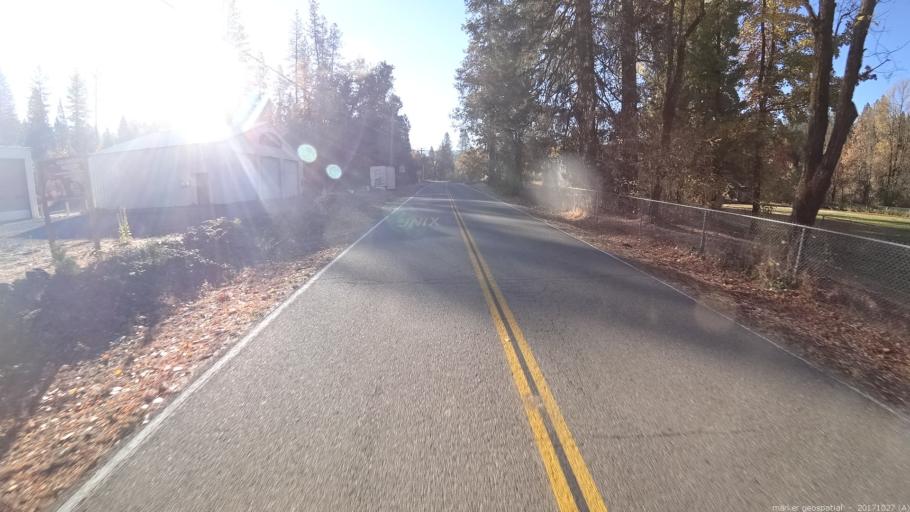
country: US
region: California
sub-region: Shasta County
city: Burney
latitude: 41.0153
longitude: -121.9064
